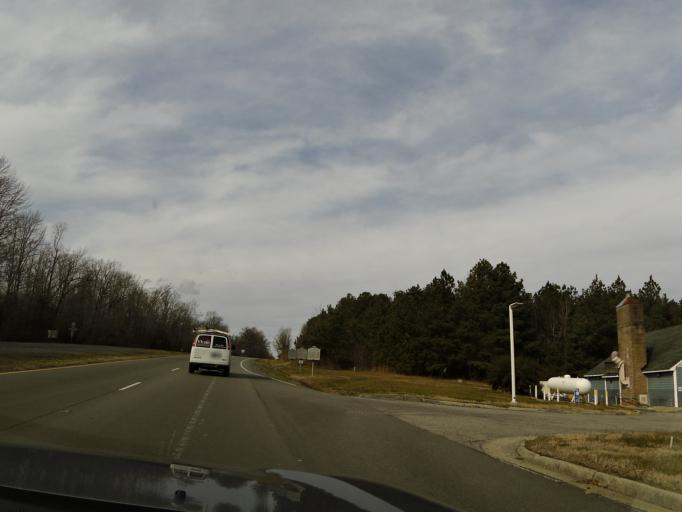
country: US
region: Virginia
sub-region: Chesterfield County
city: Enon
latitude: 37.3195
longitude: -77.3065
